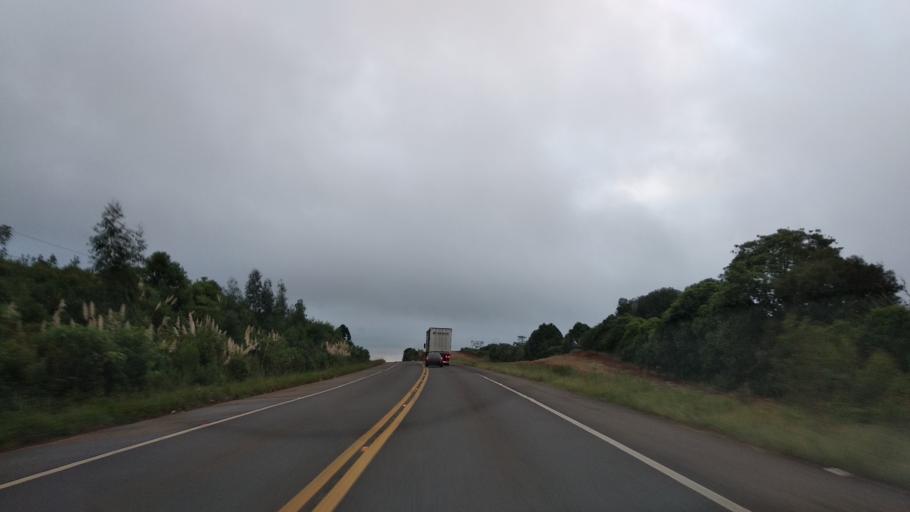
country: BR
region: Santa Catarina
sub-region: Campos Novos
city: Campos Novos
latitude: -27.3841
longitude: -51.1051
